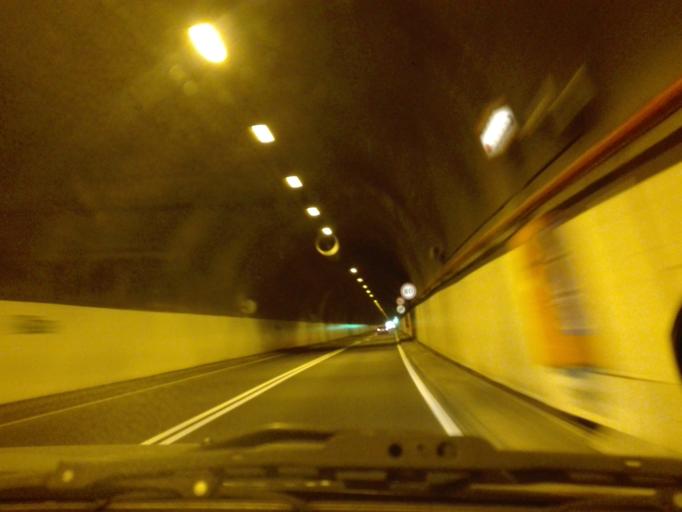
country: PT
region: Madeira
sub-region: Machico
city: Machico
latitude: 32.7338
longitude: -16.7923
